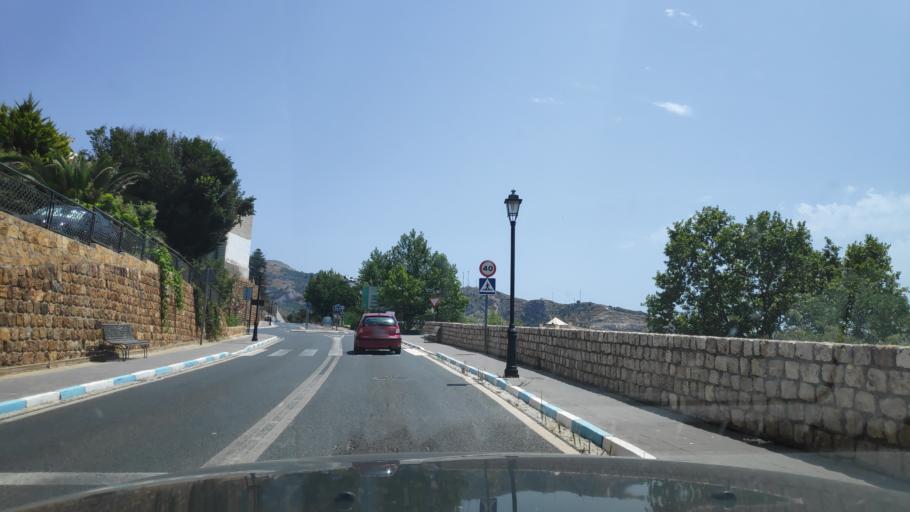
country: ES
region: Andalusia
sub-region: Provincia de Granada
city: Lanjaron
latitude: 36.9164
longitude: -3.4854
